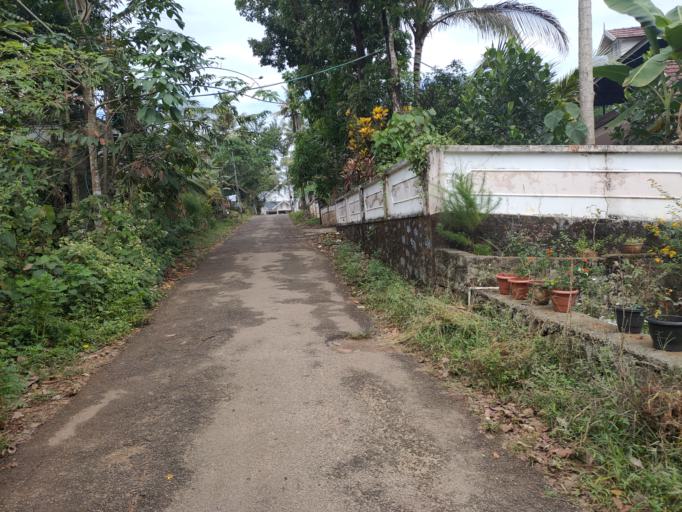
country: IN
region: Kerala
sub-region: Ernakulam
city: Kotamangalam
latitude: 10.0049
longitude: 76.6441
